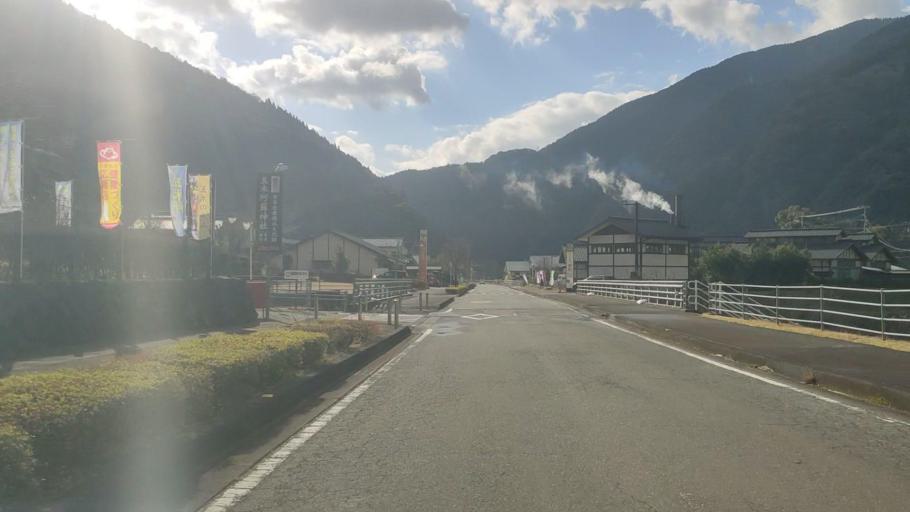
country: JP
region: Kumamoto
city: Hitoyoshi
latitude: 32.3983
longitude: 130.8266
